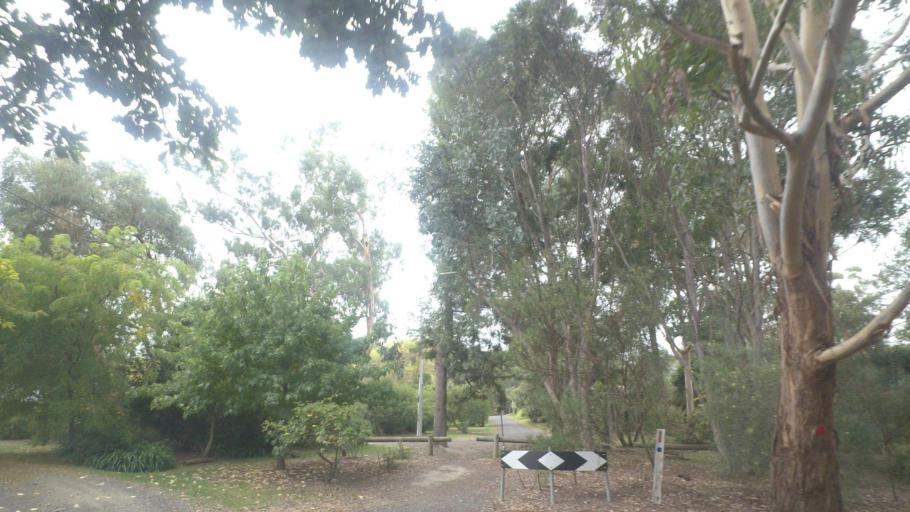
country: AU
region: Victoria
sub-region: Nillumbik
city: North Warrandyte
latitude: -37.7439
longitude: 145.2058
